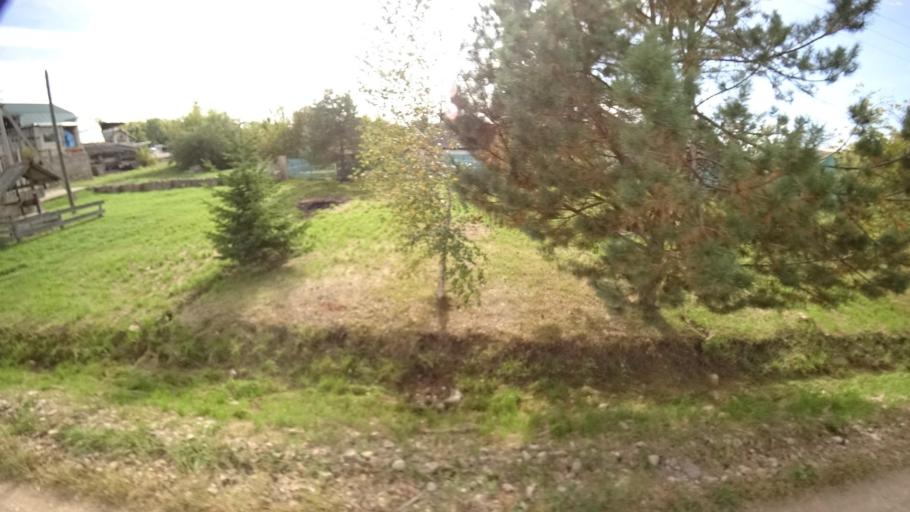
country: RU
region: Primorskiy
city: Dostoyevka
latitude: 44.3025
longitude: 133.4626
